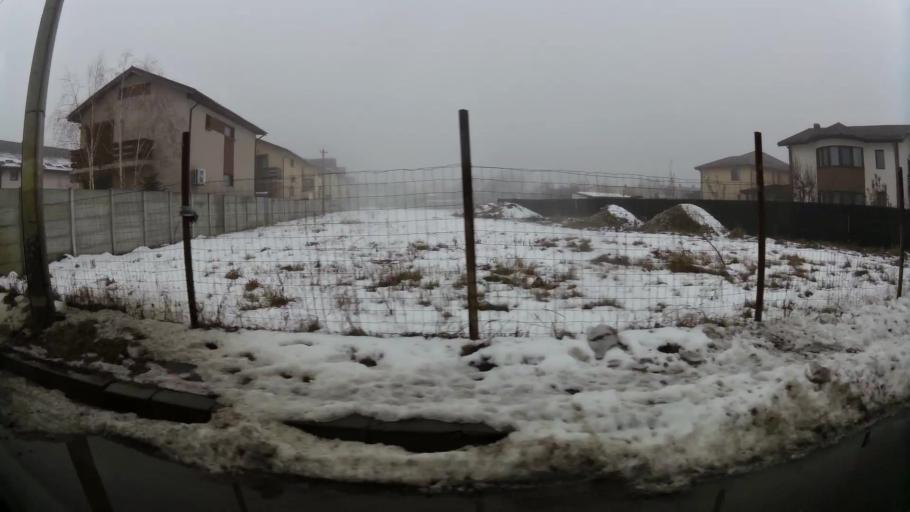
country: RO
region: Ilfov
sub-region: Comuna Chiajna
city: Chiajna
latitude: 44.4560
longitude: 25.9732
